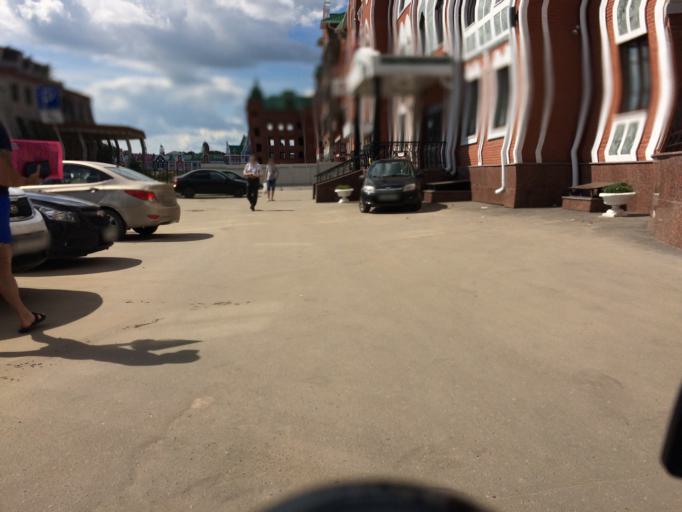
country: RU
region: Mariy-El
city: Yoshkar-Ola
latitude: 56.6295
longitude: 47.9058
